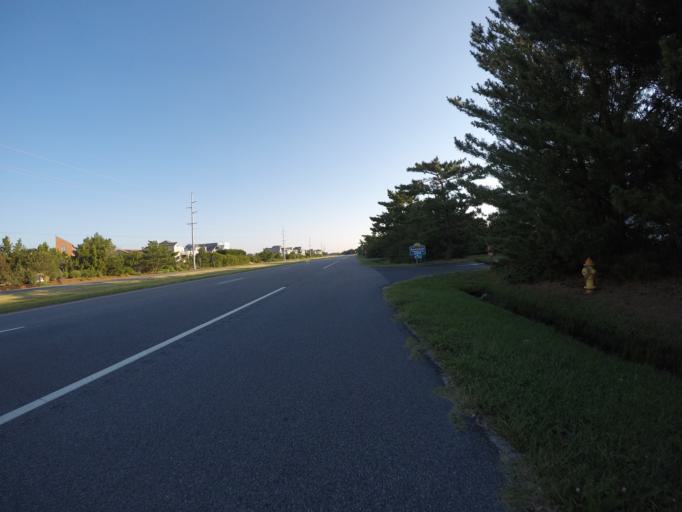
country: US
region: Delaware
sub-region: Sussex County
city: Bethany Beach
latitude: 38.4796
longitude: -75.0519
